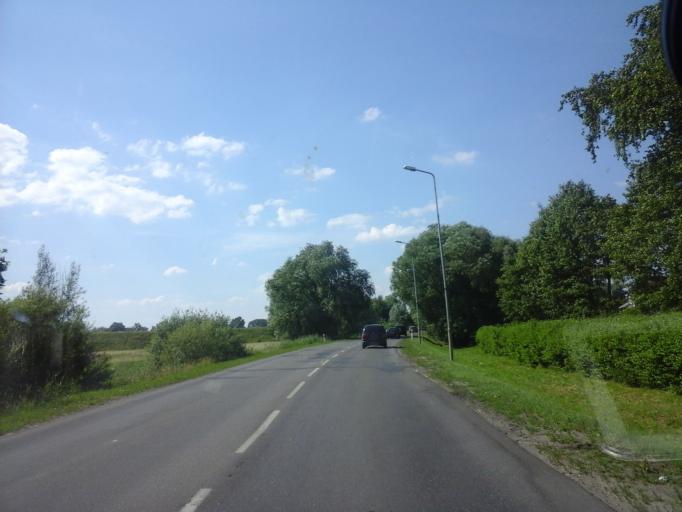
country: PL
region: West Pomeranian Voivodeship
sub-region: Powiat bialogardzki
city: Bialogard
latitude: 54.0000
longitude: 15.9895
